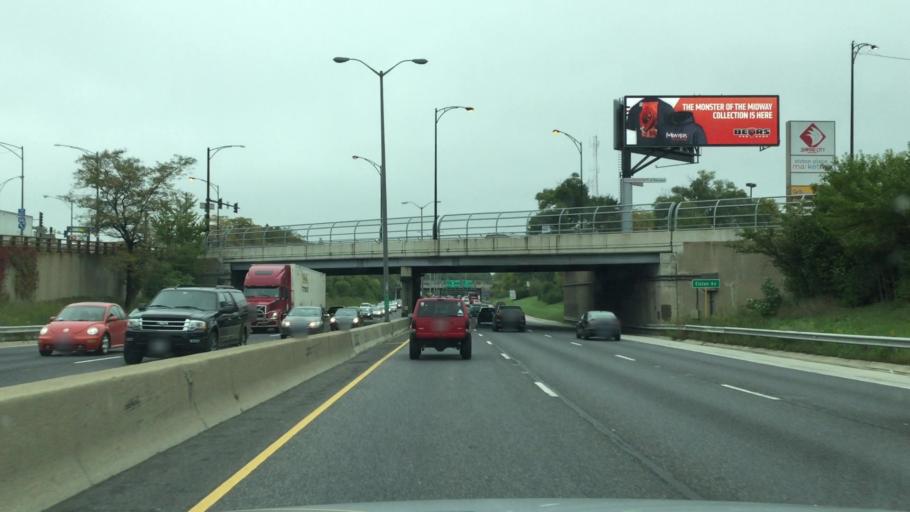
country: US
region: Illinois
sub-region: Cook County
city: Lincolnwood
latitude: 41.9719
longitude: -87.7474
